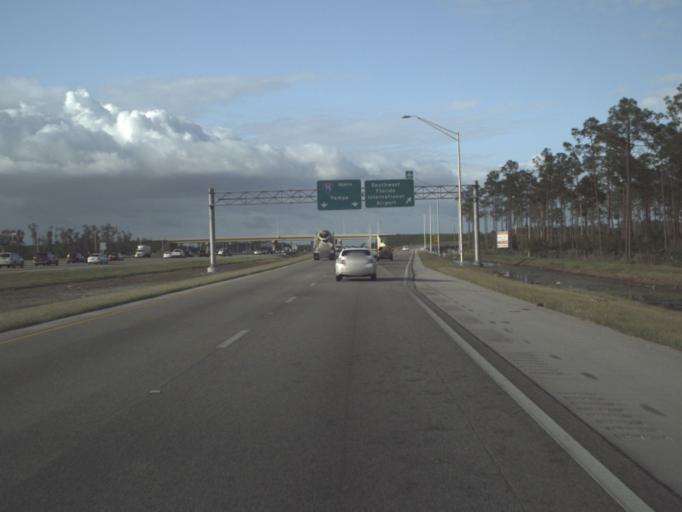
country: US
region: Florida
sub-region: Lee County
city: Three Oaks
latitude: 26.5062
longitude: -81.7940
